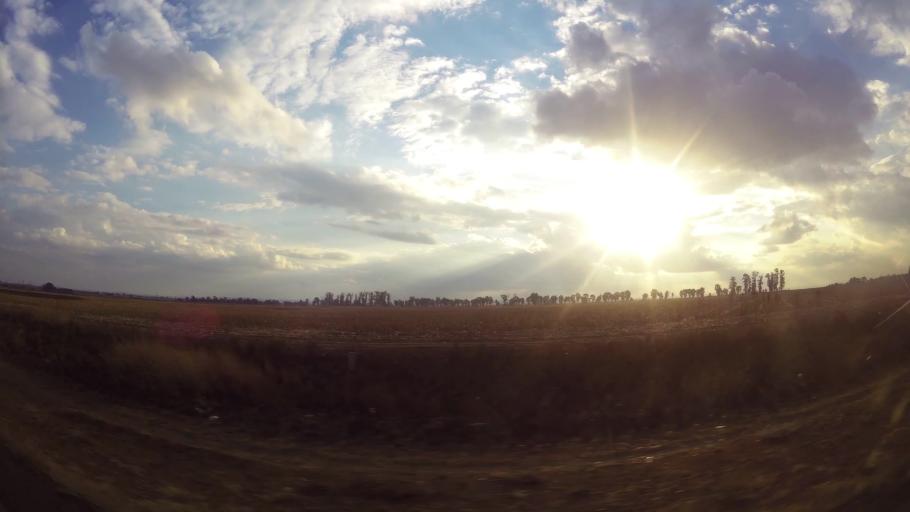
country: ZA
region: Gauteng
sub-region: Sedibeng District Municipality
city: Vanderbijlpark
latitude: -26.6508
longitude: 27.8032
